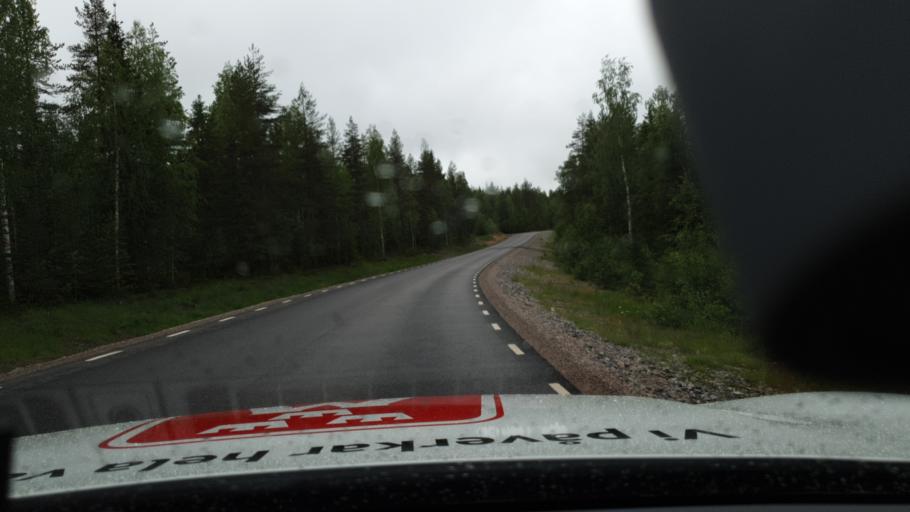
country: SE
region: Norrbotten
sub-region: Overtornea Kommun
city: OEvertornea
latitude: 66.4603
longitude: 23.4716
